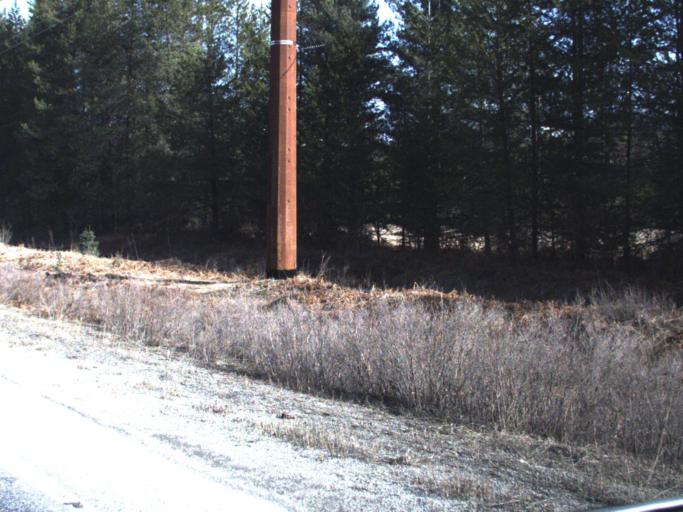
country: CA
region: British Columbia
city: Fruitvale
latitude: 48.6624
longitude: -117.3922
